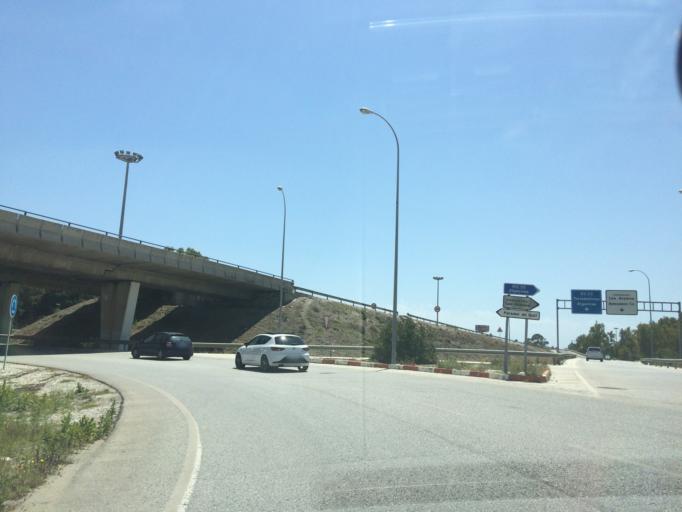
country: ES
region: Andalusia
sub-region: Provincia de Malaga
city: Torremolinos
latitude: 36.6532
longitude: -4.4793
